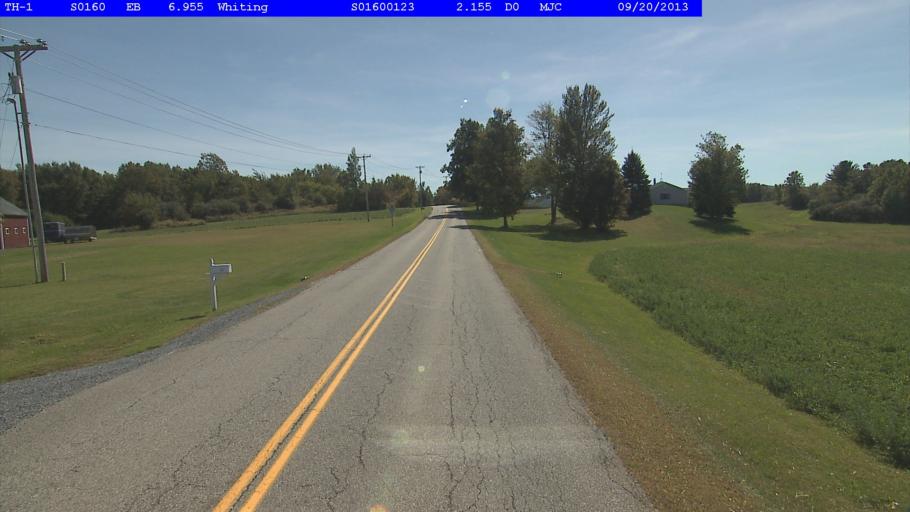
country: US
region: Vermont
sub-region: Rutland County
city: Brandon
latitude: 43.8578
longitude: -73.1852
